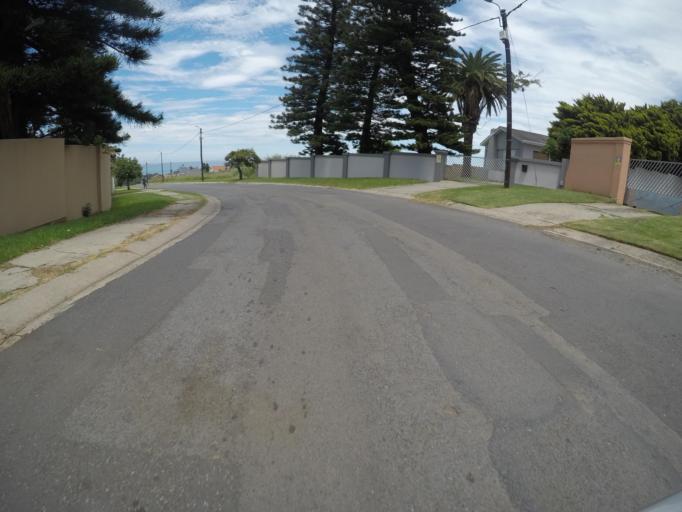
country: ZA
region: Eastern Cape
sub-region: Buffalo City Metropolitan Municipality
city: East London
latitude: -33.0384
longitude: 27.8572
